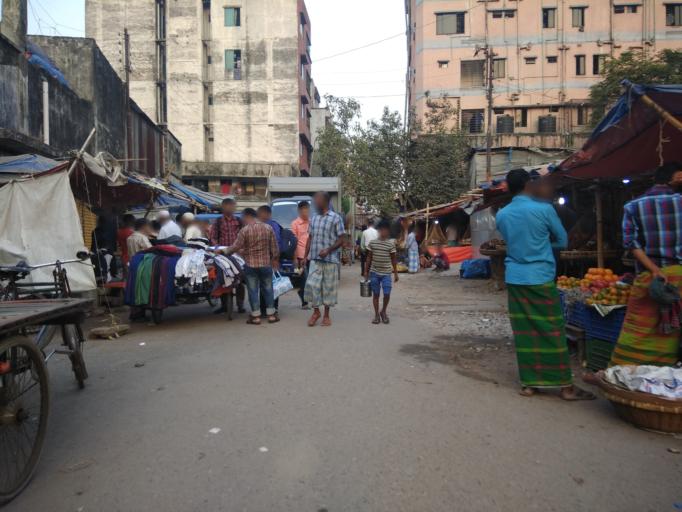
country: BD
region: Dhaka
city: Azimpur
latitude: 23.7663
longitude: 90.3595
